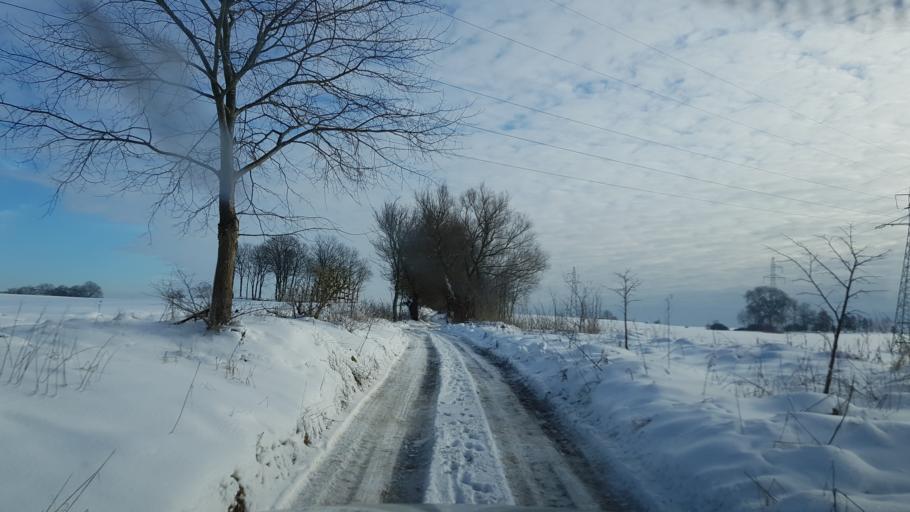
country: PL
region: West Pomeranian Voivodeship
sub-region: Powiat drawski
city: Drawsko Pomorskie
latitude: 53.5337
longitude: 15.7762
